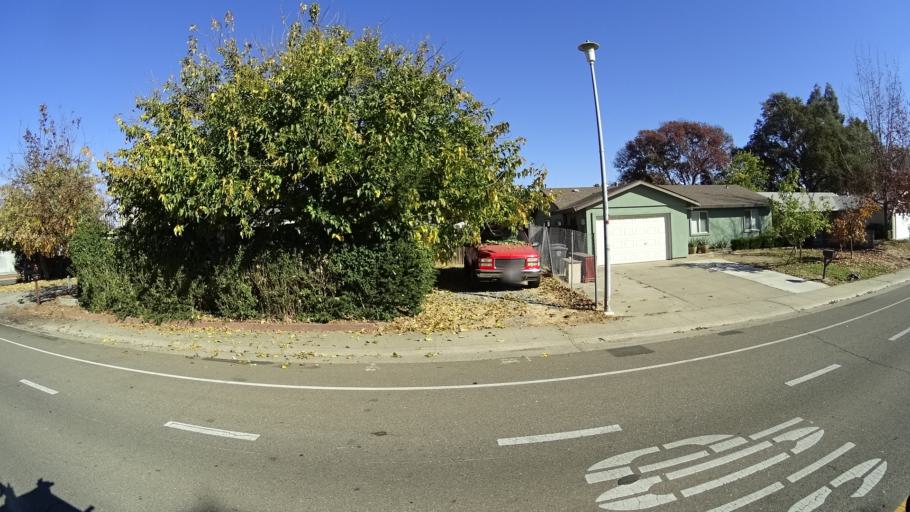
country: US
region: California
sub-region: Sacramento County
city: Antelope
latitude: 38.7178
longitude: -121.3131
